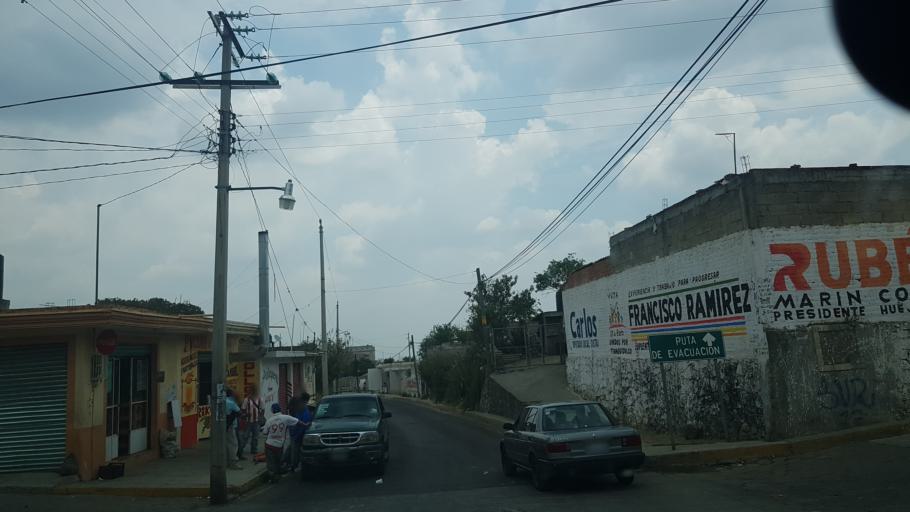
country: MX
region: Puebla
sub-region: Huejotzingo
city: San Miguel Tianguizolco
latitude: 19.1593
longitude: -98.4396
